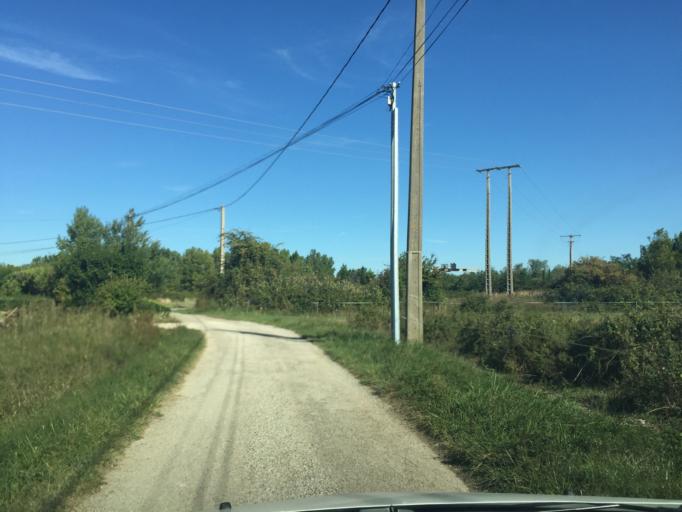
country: FR
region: Provence-Alpes-Cote d'Azur
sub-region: Departement du Vaucluse
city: Piolenc
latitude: 44.1467
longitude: 4.7738
